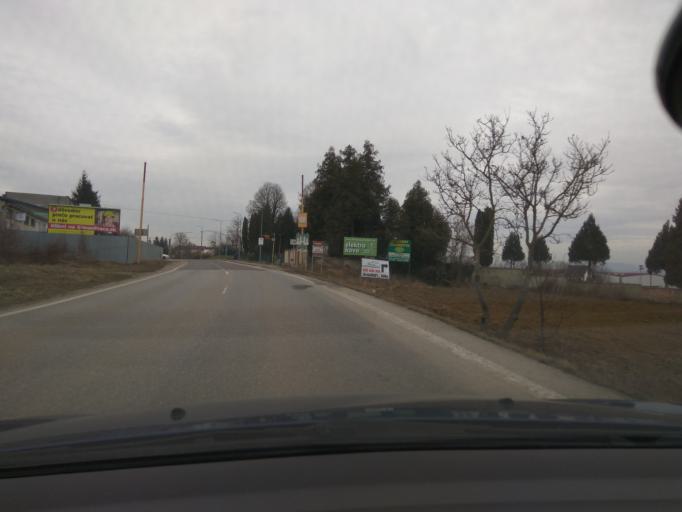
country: SK
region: Nitriansky
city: Ilava
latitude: 49.0014
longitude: 18.2423
